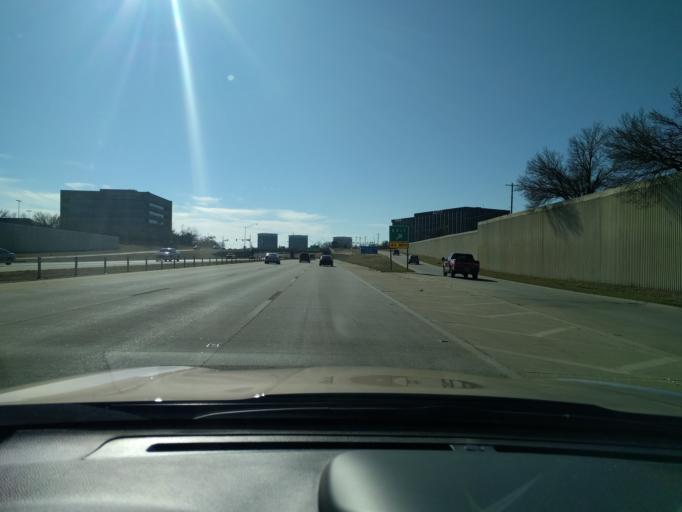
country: US
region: Oklahoma
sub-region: Oklahoma County
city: Nichols Hills
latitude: 35.5397
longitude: -97.5772
